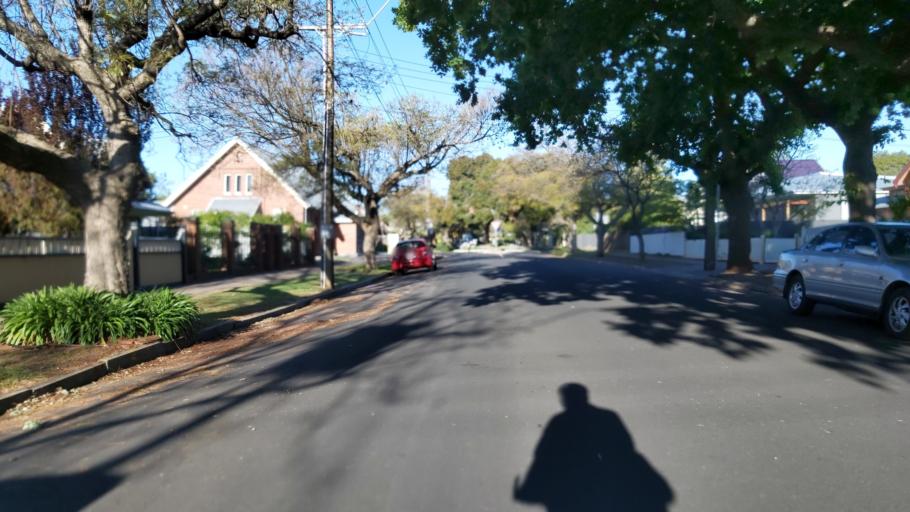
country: AU
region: South Australia
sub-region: Unley
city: Unley
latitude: -34.9452
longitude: 138.5955
